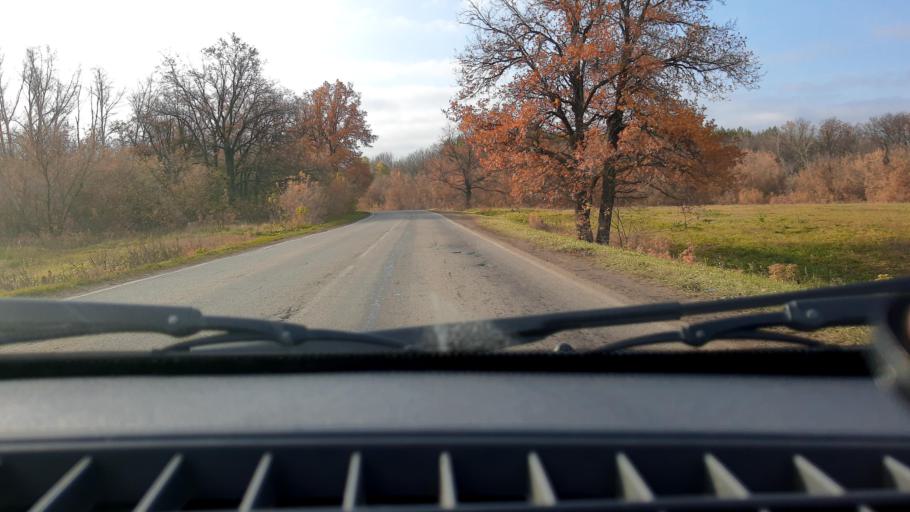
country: RU
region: Bashkortostan
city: Ufa
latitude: 54.5670
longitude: 55.9634
